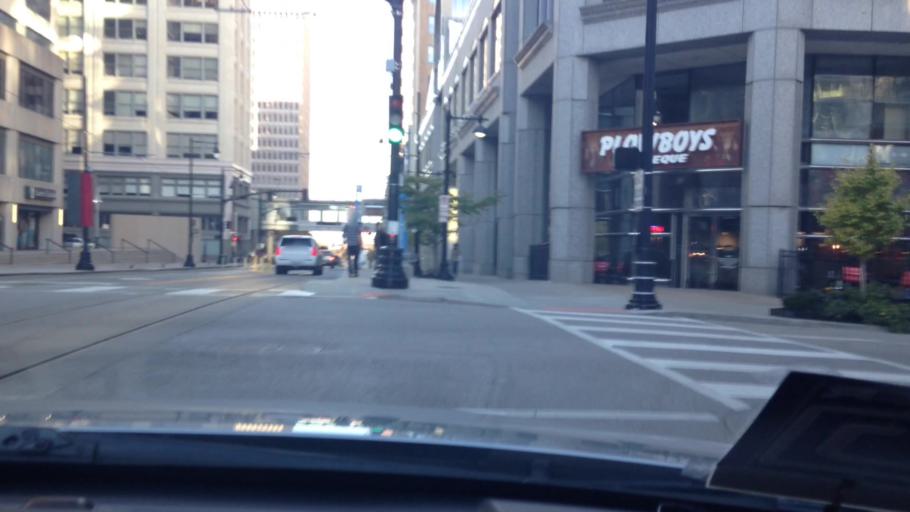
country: US
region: Missouri
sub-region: Jackson County
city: Kansas City
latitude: 39.0998
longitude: -94.5832
